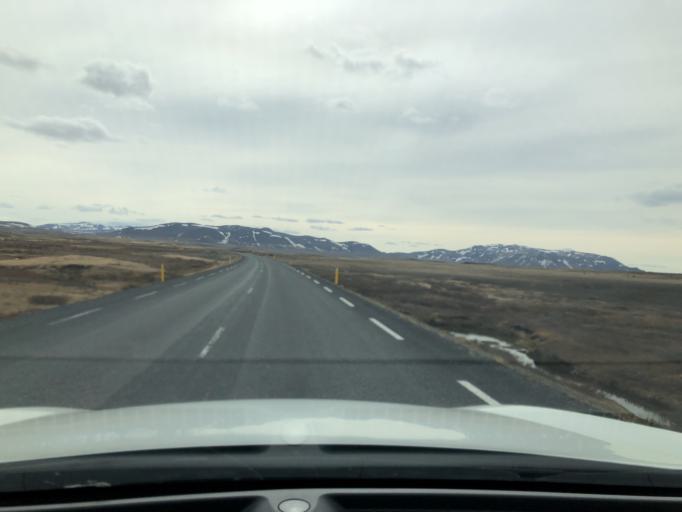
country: IS
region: Northeast
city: Laugar
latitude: 65.5994
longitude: -16.1355
